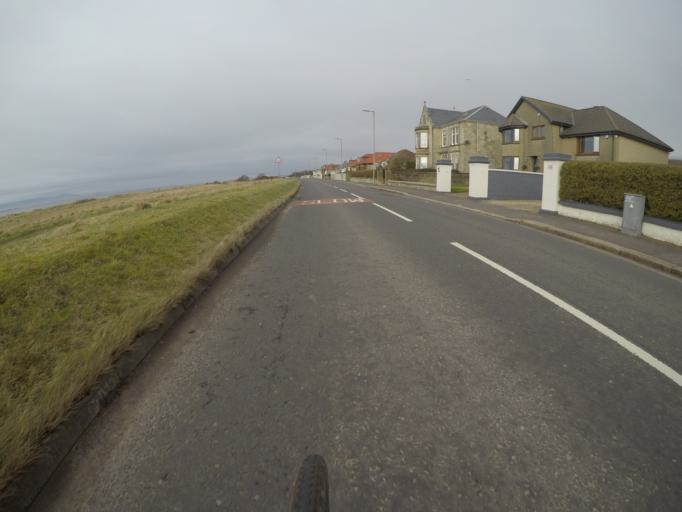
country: GB
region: Scotland
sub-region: North Ayrshire
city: Ardrossan
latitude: 55.6492
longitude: -4.8151
